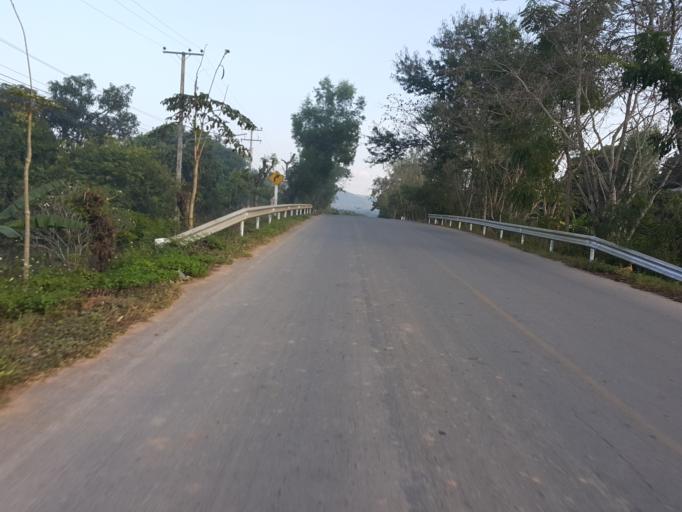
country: TH
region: Lamphun
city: Thung Hua Chang
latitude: 17.9804
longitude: 99.0378
